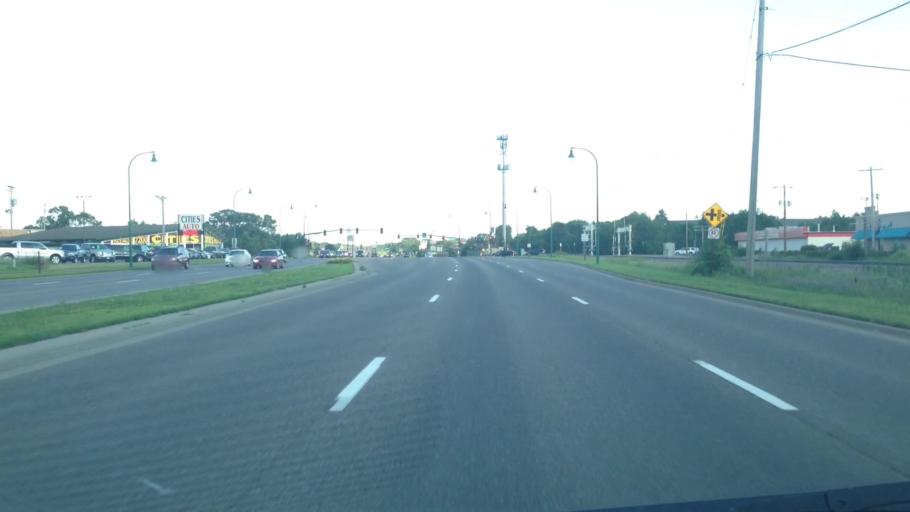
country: US
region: Minnesota
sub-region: Hennepin County
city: Crystal
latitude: 45.0565
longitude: -93.3598
